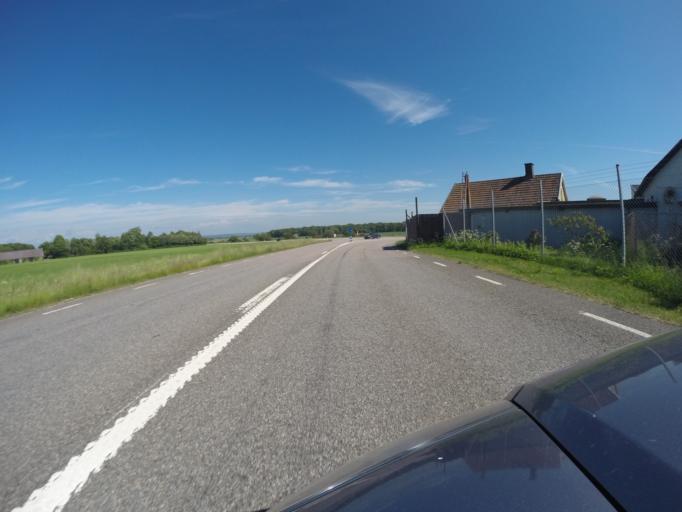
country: SE
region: Skane
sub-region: Helsingborg
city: Hyllinge
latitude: 56.1004
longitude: 12.8125
